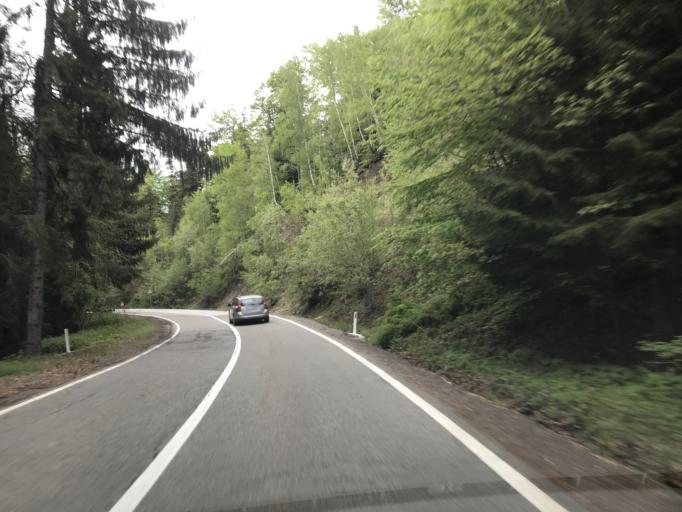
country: RO
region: Sibiu
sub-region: Comuna Cartisoara
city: Cartisoara
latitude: 45.6689
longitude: 24.5930
